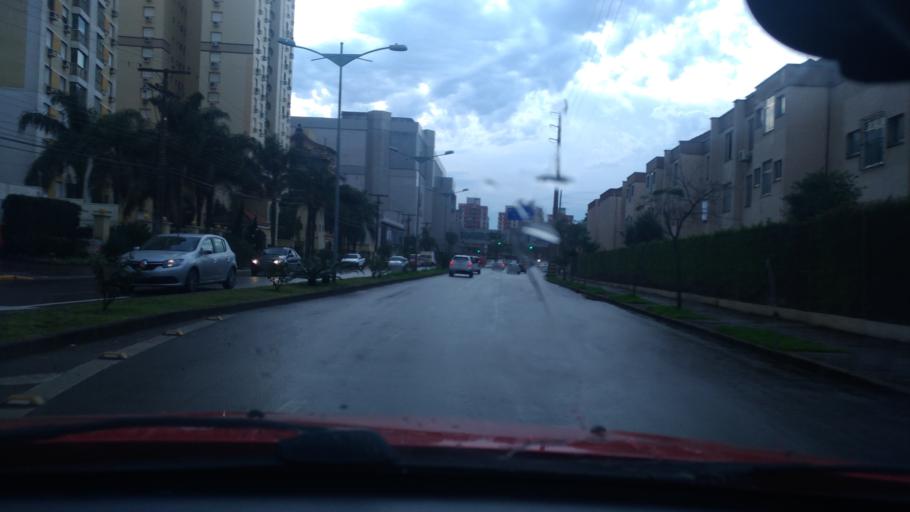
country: BR
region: Rio Grande do Sul
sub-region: Porto Alegre
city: Porto Alegre
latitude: -30.0133
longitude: -51.1635
